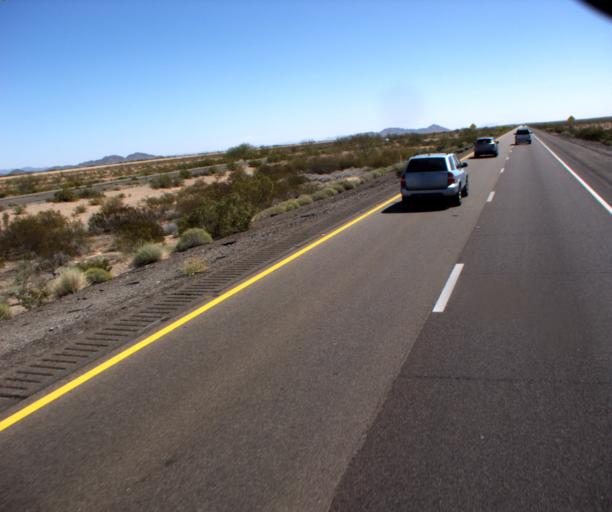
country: US
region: Arizona
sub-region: La Paz County
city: Salome
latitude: 33.6039
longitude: -113.5872
